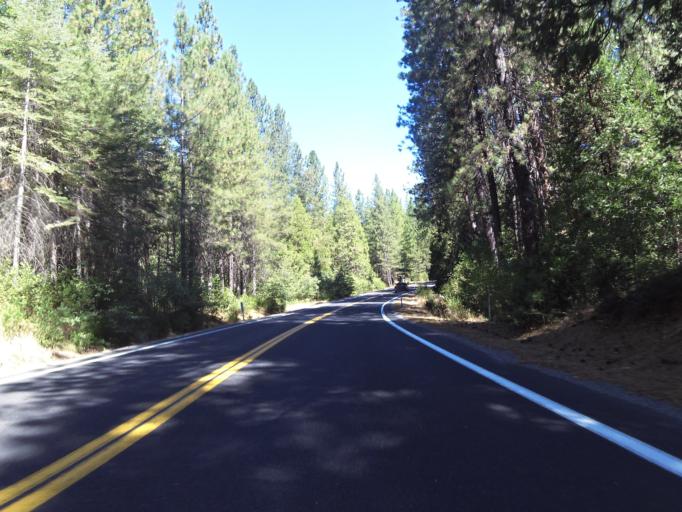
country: US
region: California
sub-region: Calaveras County
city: Arnold
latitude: 38.2165
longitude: -120.3709
